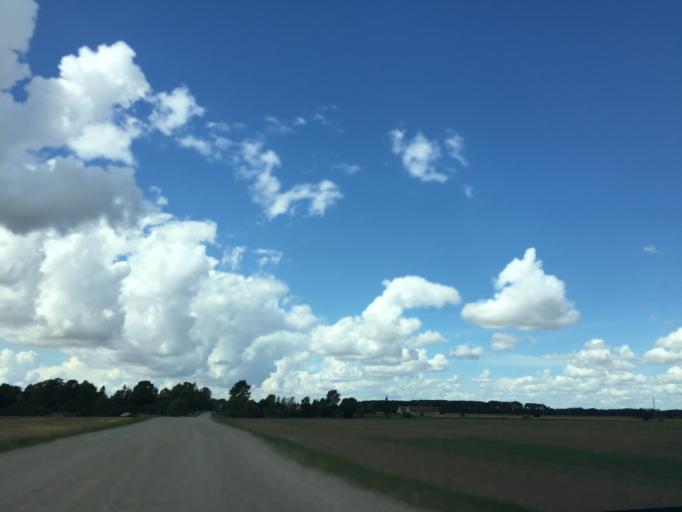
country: LV
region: Rundales
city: Pilsrundale
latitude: 56.3552
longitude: 24.0011
